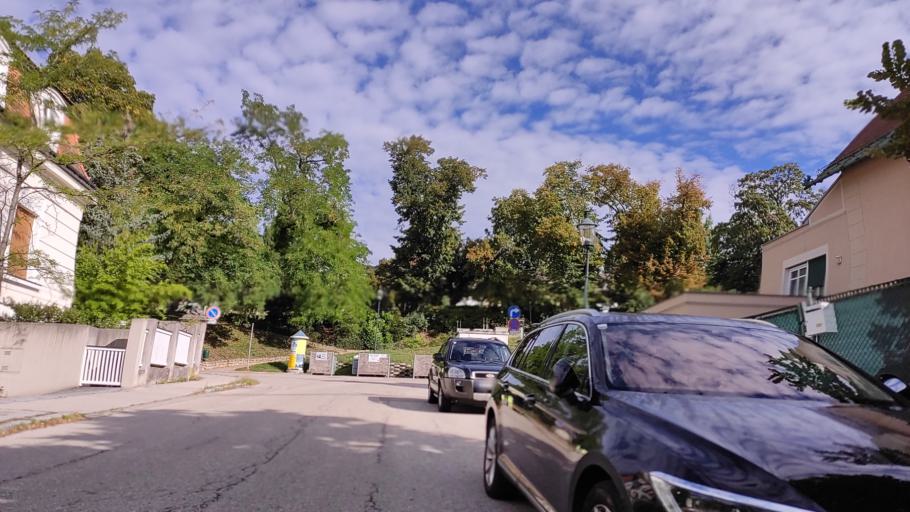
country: AT
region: Lower Austria
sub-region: Politischer Bezirk Baden
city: Baden
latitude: 48.0092
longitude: 16.2211
